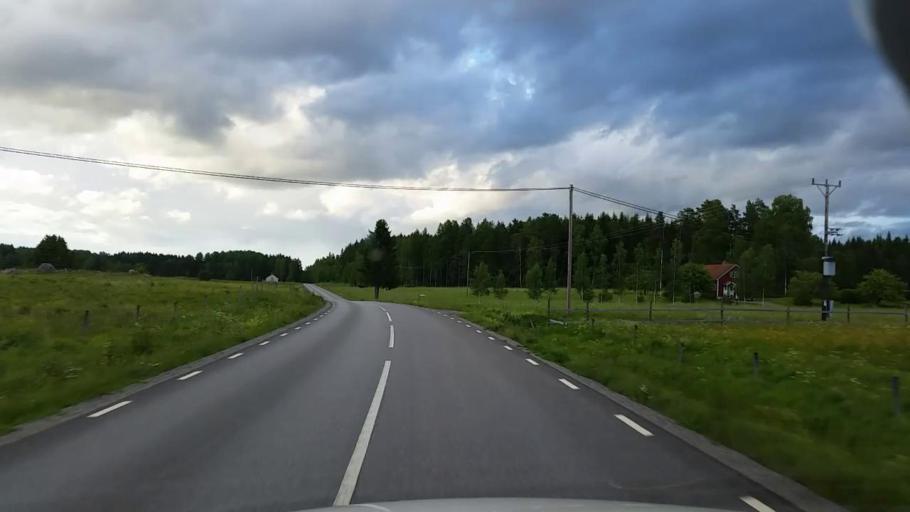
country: SE
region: Vaestmanland
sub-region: Kopings Kommun
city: Kolsva
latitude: 59.7635
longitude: 15.8457
